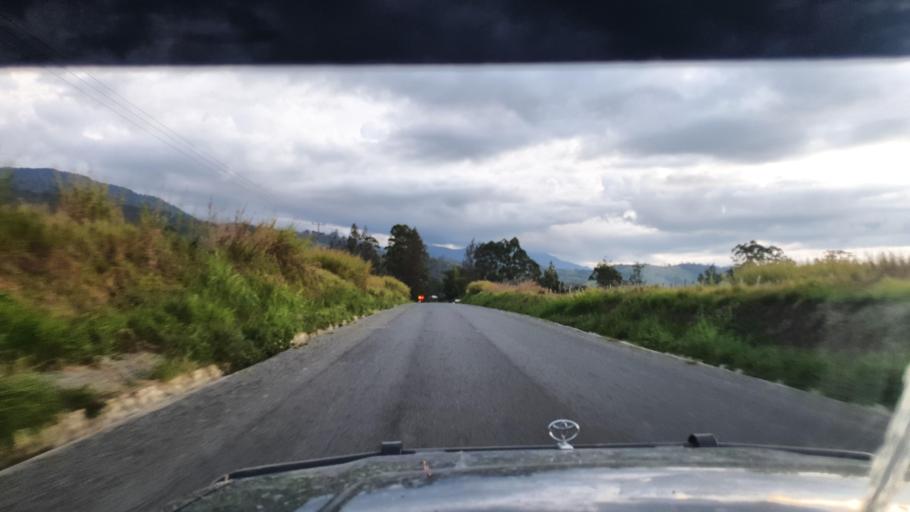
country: PG
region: Jiwaka
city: Minj
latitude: -5.8425
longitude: 144.5322
